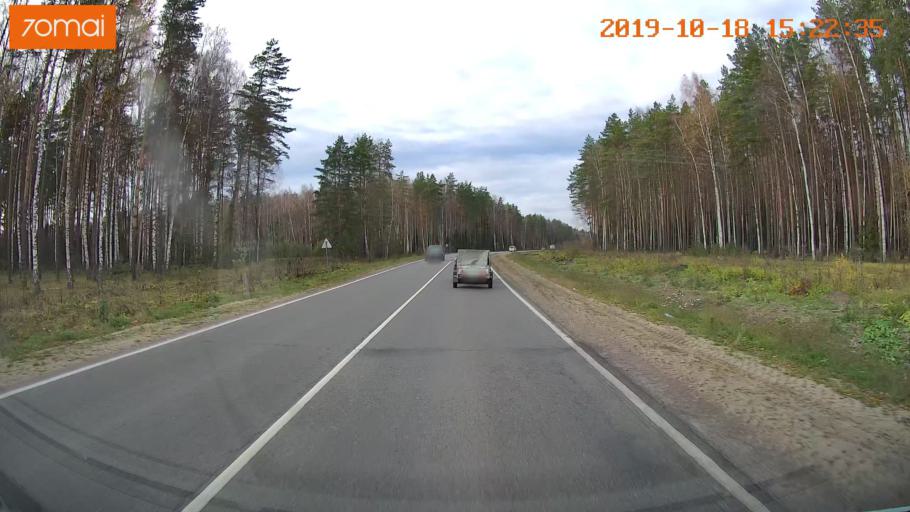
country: RU
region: Vladimir
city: Anopino
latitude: 55.7091
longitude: 40.7300
